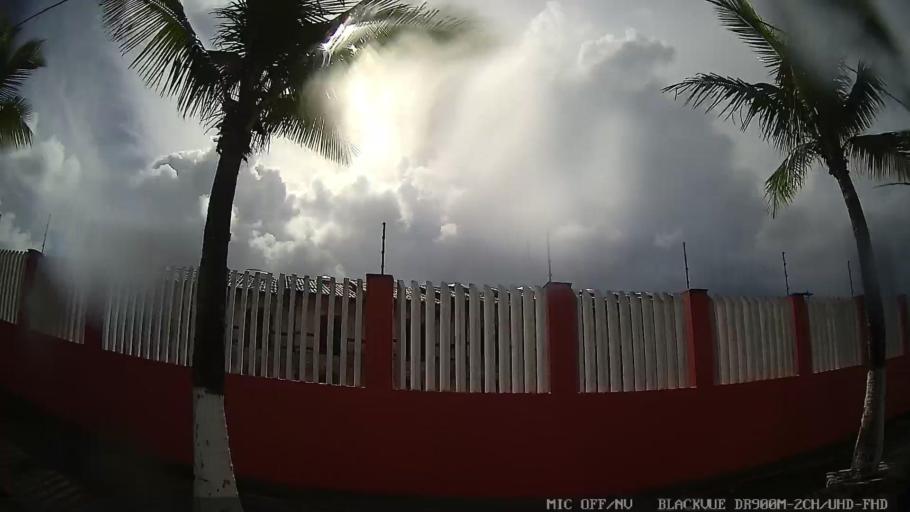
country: BR
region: Sao Paulo
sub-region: Itanhaem
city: Itanhaem
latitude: -24.2387
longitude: -46.8731
